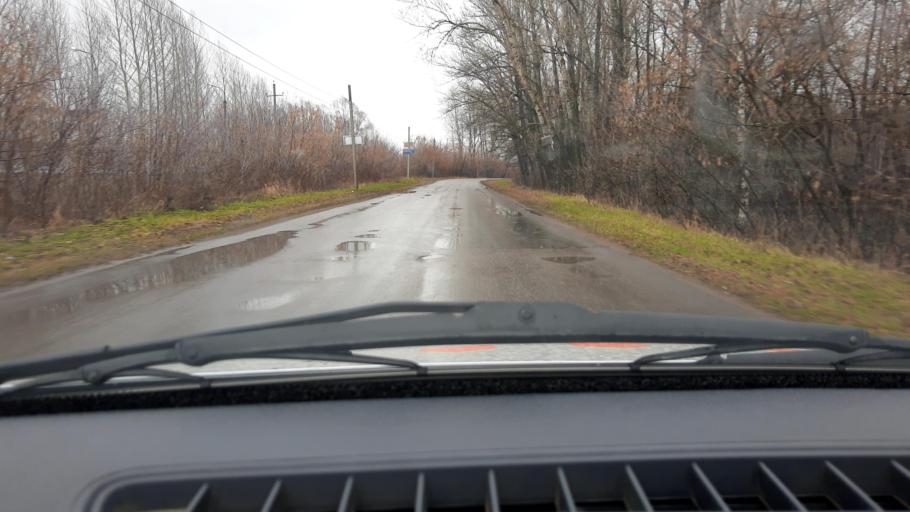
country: RU
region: Bashkortostan
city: Ufa
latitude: 54.8081
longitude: 56.1849
